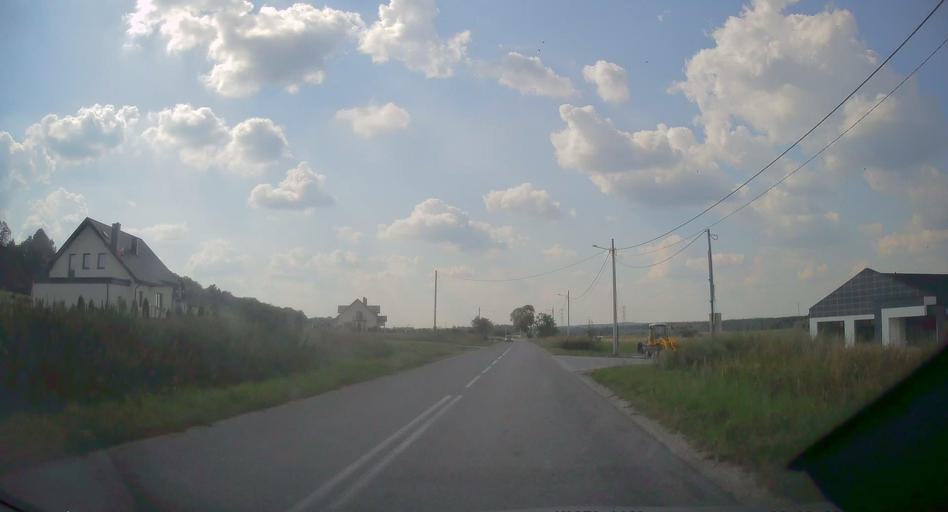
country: PL
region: Swietokrzyskie
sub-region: Powiat jedrzejowski
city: Malogoszcz
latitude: 50.8603
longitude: 20.3455
